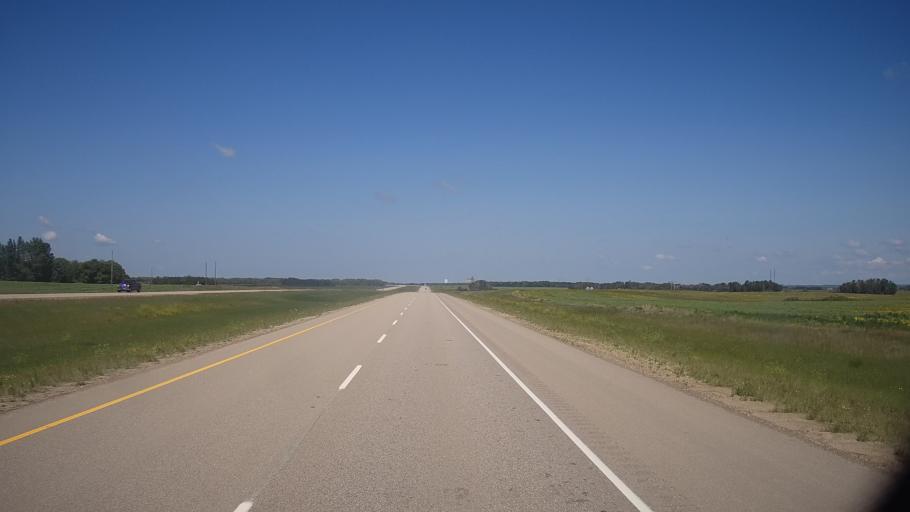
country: CA
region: Saskatchewan
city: Saskatoon
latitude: 52.0033
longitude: -106.3381
